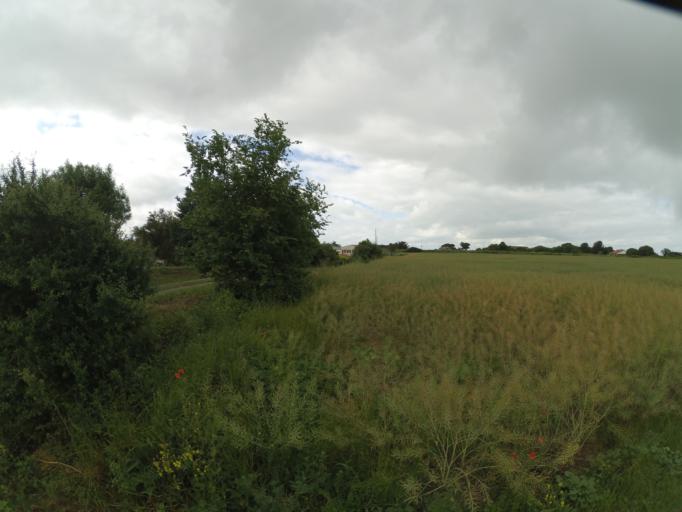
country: FR
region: Poitou-Charentes
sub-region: Departement de la Charente-Maritime
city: Aytre
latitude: 46.1313
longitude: -1.1310
